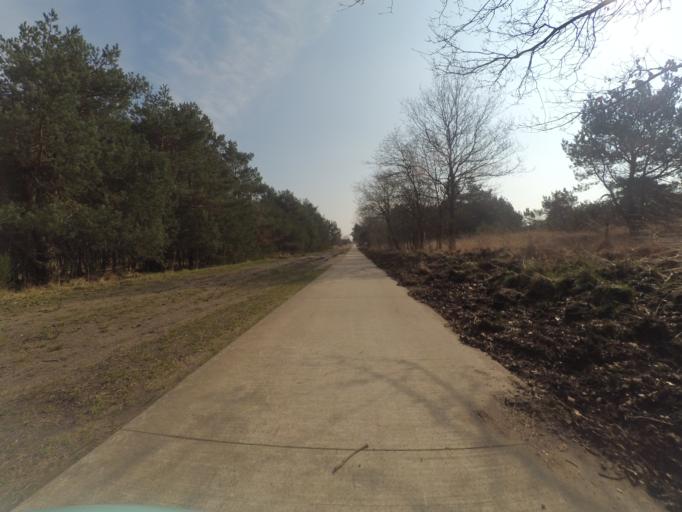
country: NL
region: Gelderland
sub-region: Gemeente Ede
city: Harskamp
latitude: 52.1684
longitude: 5.8236
